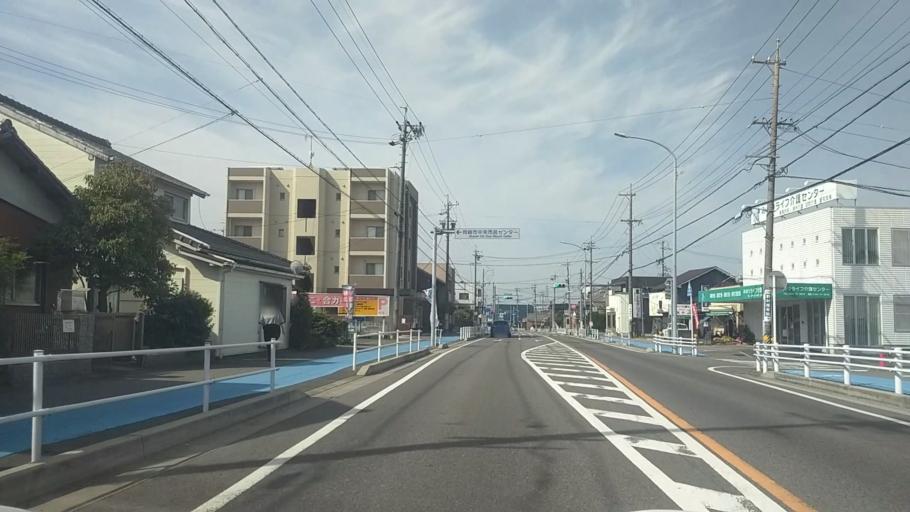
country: JP
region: Aichi
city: Okazaki
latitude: 34.9479
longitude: 137.1573
